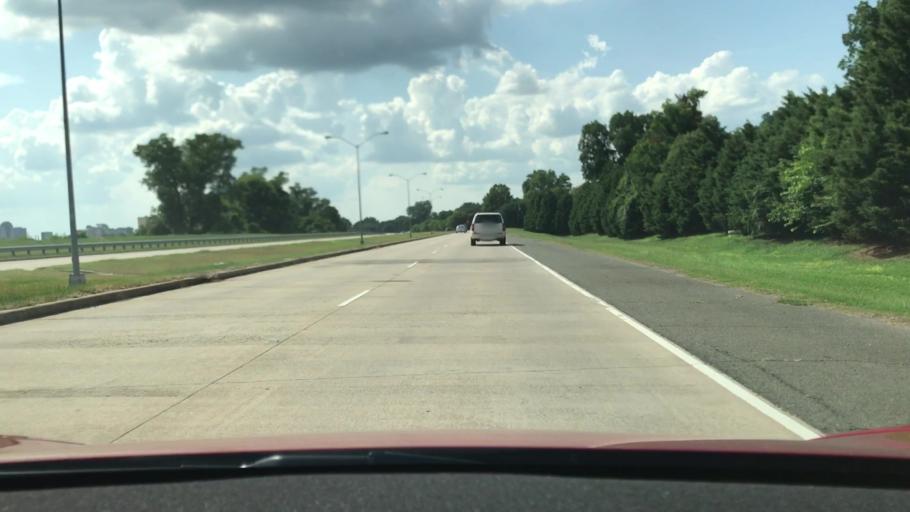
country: US
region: Louisiana
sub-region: Bossier Parish
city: Bossier City
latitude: 32.5053
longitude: -93.7106
